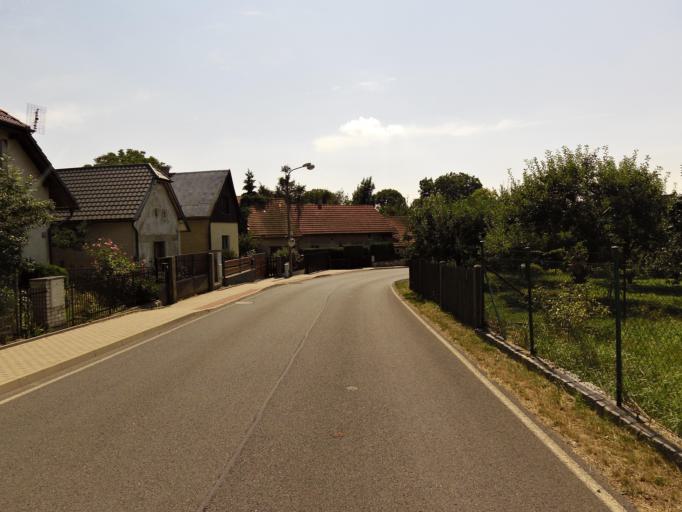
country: CZ
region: Central Bohemia
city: Mukarov
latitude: 49.9542
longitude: 14.7460
